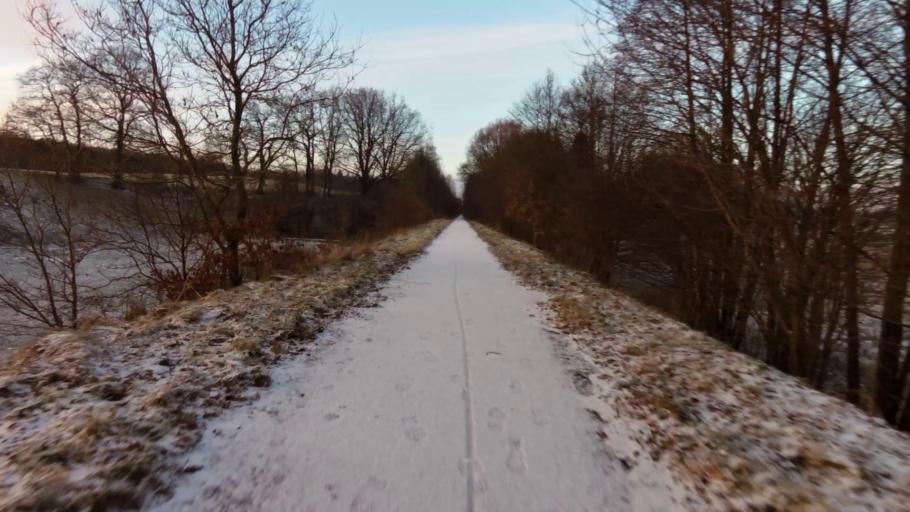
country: PL
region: West Pomeranian Voivodeship
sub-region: Powiat swidwinski
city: Polczyn-Zdroj
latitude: 53.6930
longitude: 16.0384
